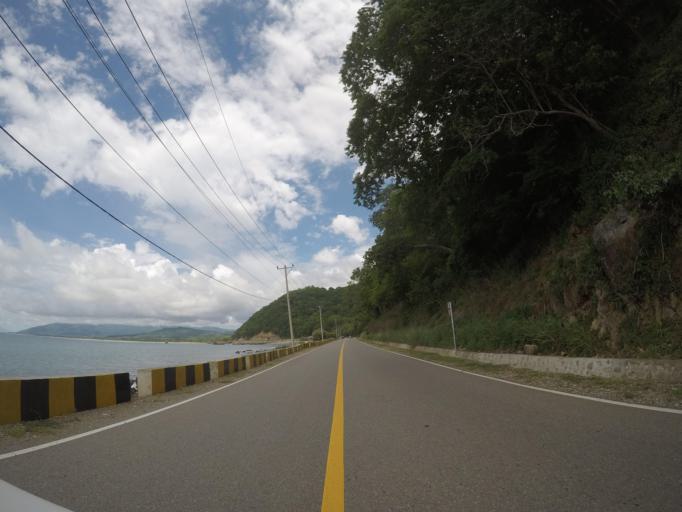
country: TL
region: Liquica
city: Maubara
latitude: -8.8047
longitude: 125.0901
